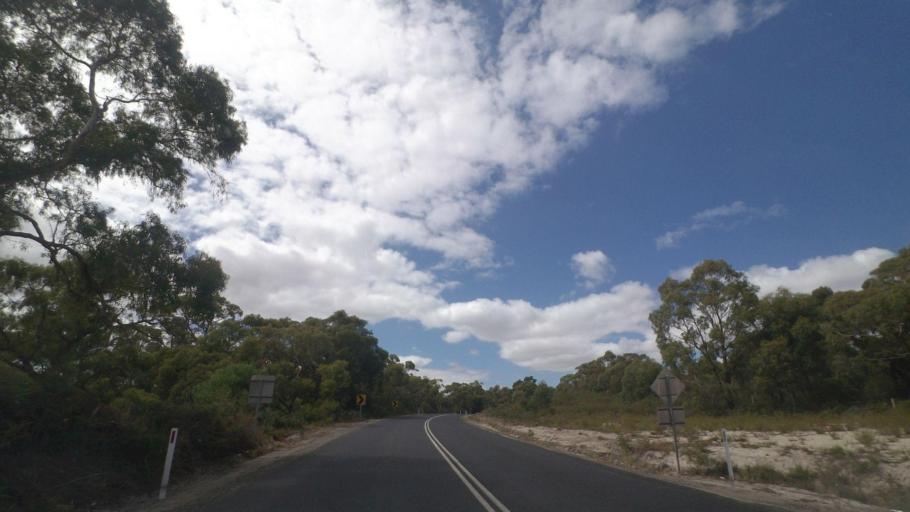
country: AU
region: Victoria
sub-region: Cardinia
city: Koo-Wee-Rup
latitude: -38.2970
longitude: 145.6306
